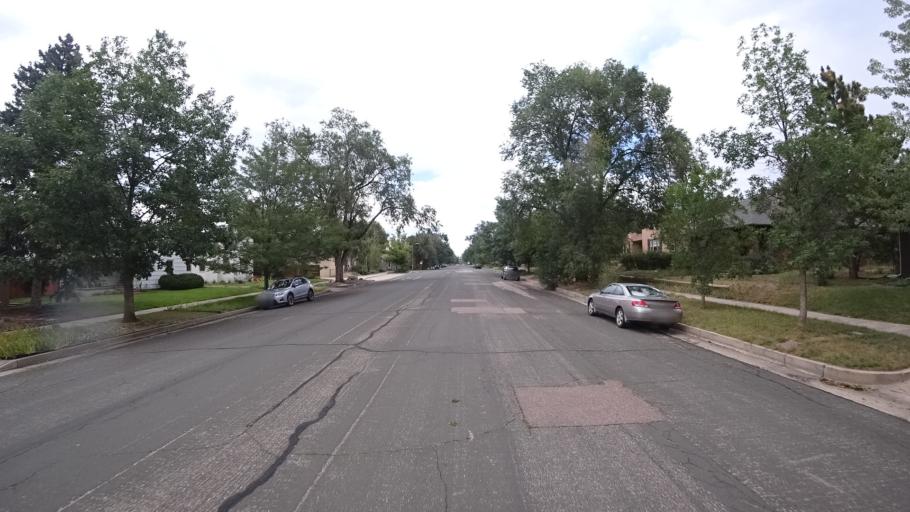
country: US
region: Colorado
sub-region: El Paso County
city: Colorado Springs
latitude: 38.8581
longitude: -104.8150
